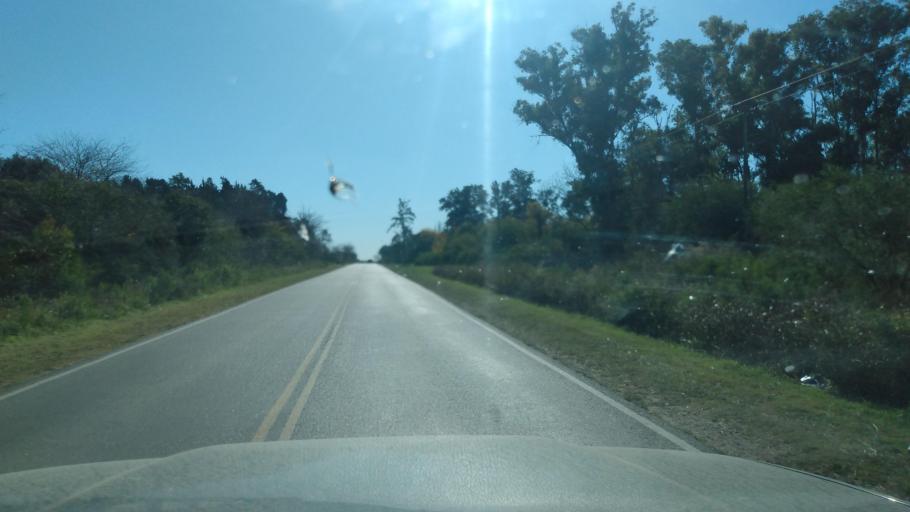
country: AR
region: Buenos Aires
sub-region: Partido de Lujan
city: Lujan
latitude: -34.5212
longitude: -59.1752
